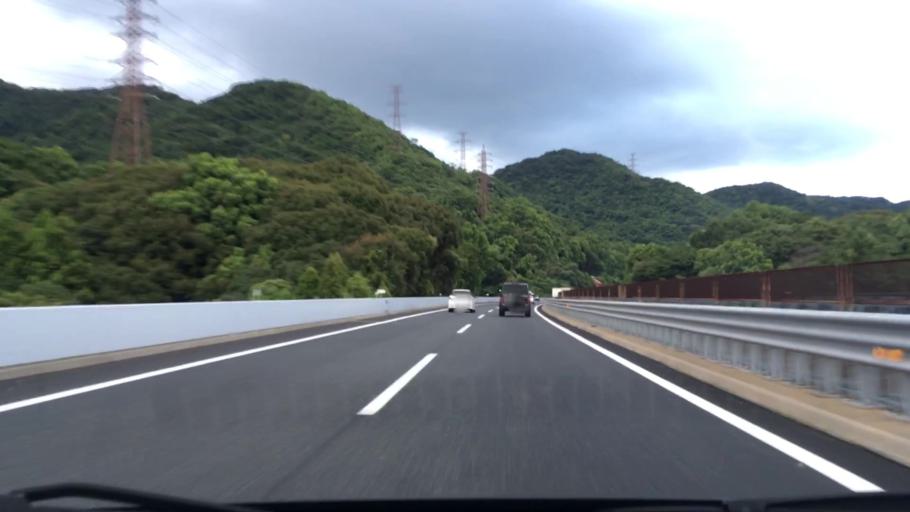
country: JP
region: Fukuoka
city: Kanda
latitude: 33.8581
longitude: 130.9392
